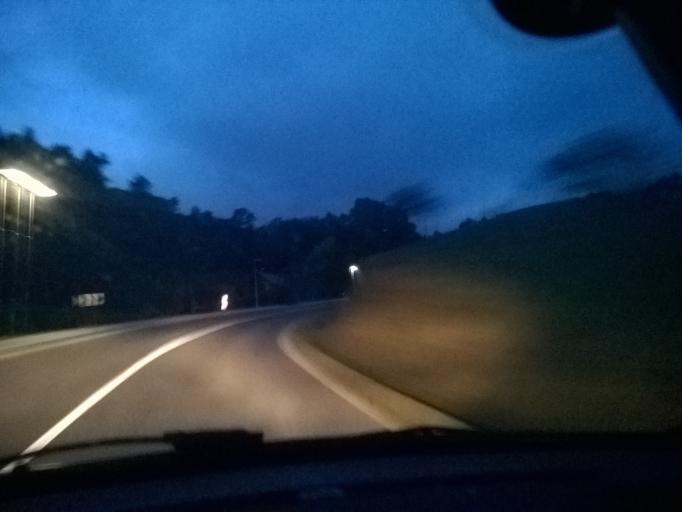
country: SI
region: Rogaska Slatina
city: Rogaska Slatina
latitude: 46.2286
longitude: 15.6614
